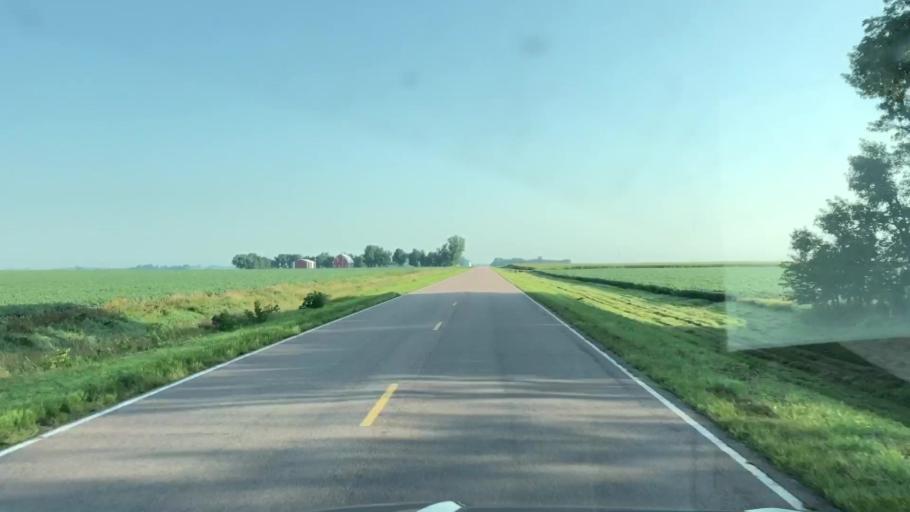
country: US
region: Iowa
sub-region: Lyon County
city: George
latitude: 43.3062
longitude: -95.9992
